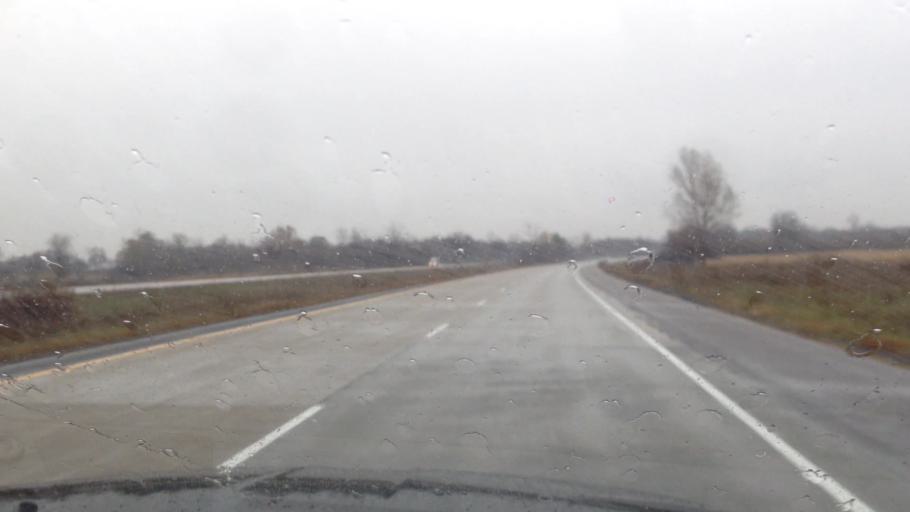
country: CA
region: Ontario
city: Casselman
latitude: 45.3799
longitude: -74.8271
